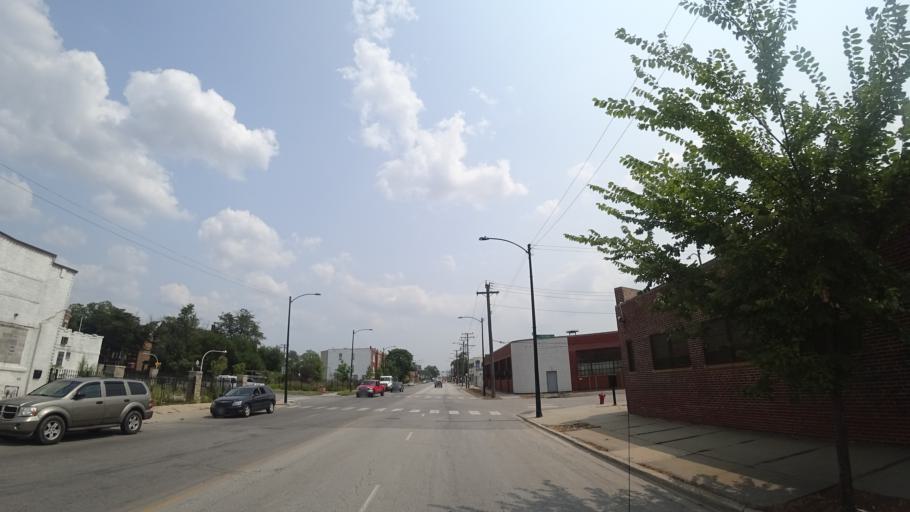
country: US
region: Illinois
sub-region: Cook County
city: Cicero
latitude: 41.8486
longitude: -87.7316
